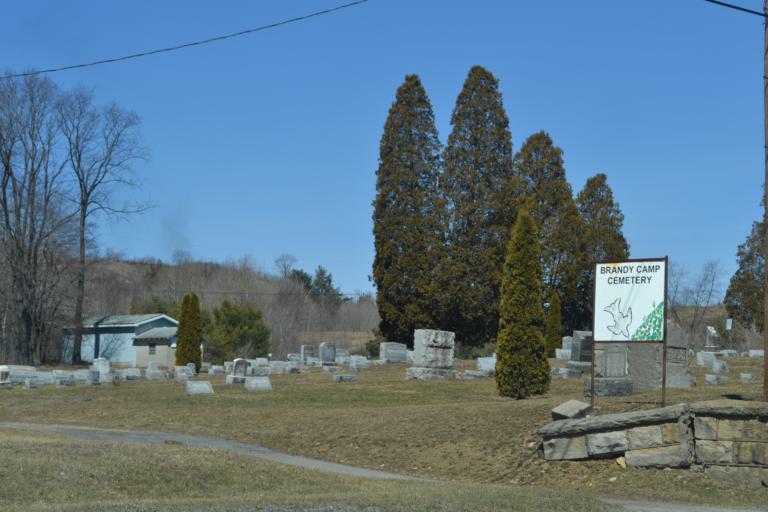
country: US
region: Pennsylvania
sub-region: Elk County
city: Ridgway
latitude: 41.3179
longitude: -78.6883
